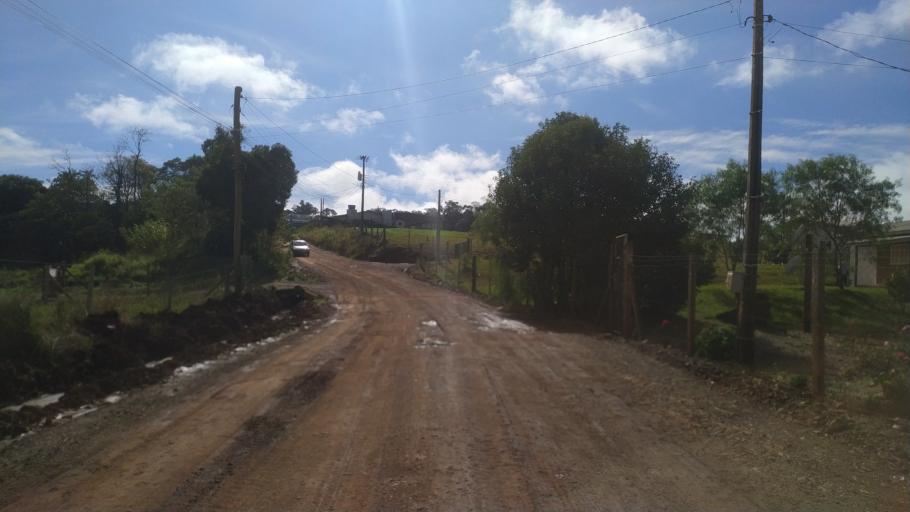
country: BR
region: Santa Catarina
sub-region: Chapeco
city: Chapeco
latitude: -27.1467
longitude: -52.5946
